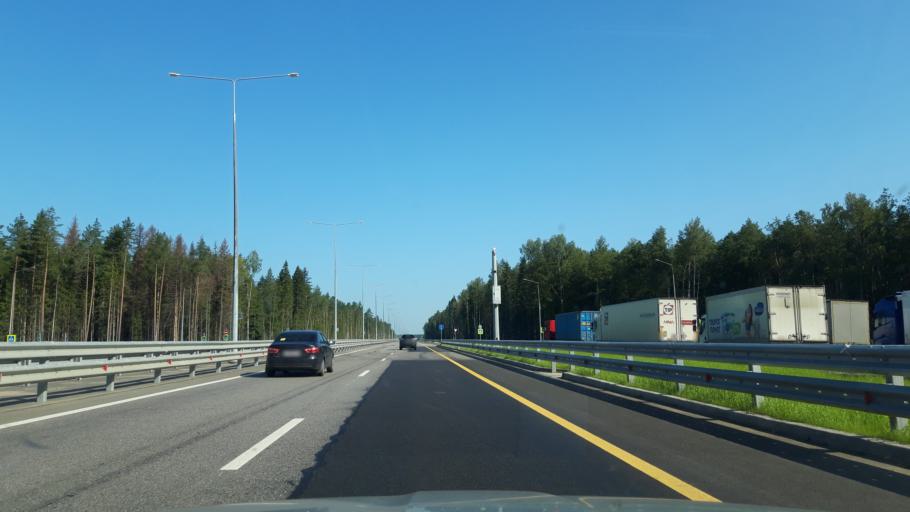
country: RU
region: Moskovskaya
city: Reshetnikovo
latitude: 56.4114
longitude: 36.5577
